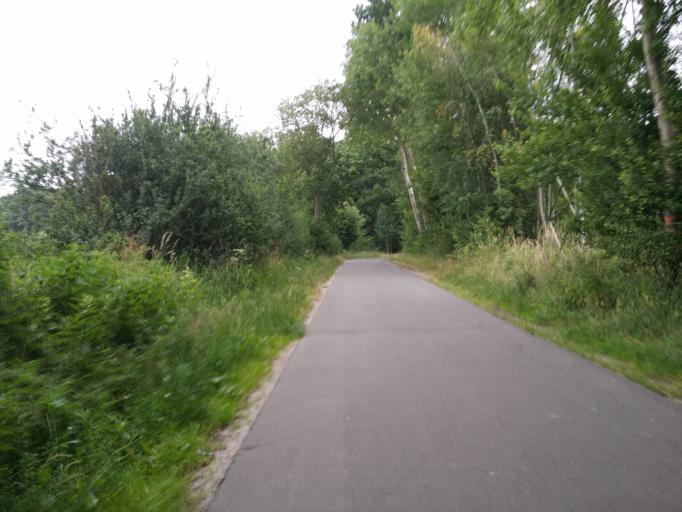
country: DE
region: Lower Saxony
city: Reppenstedt
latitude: 53.2375
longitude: 10.3533
